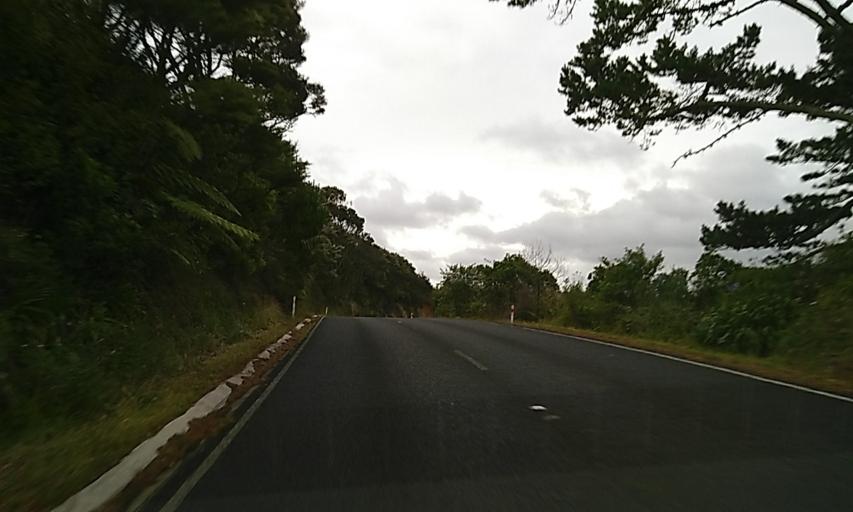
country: NZ
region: Auckland
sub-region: Auckland
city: Pukekohe East
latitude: -37.3201
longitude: 174.9298
